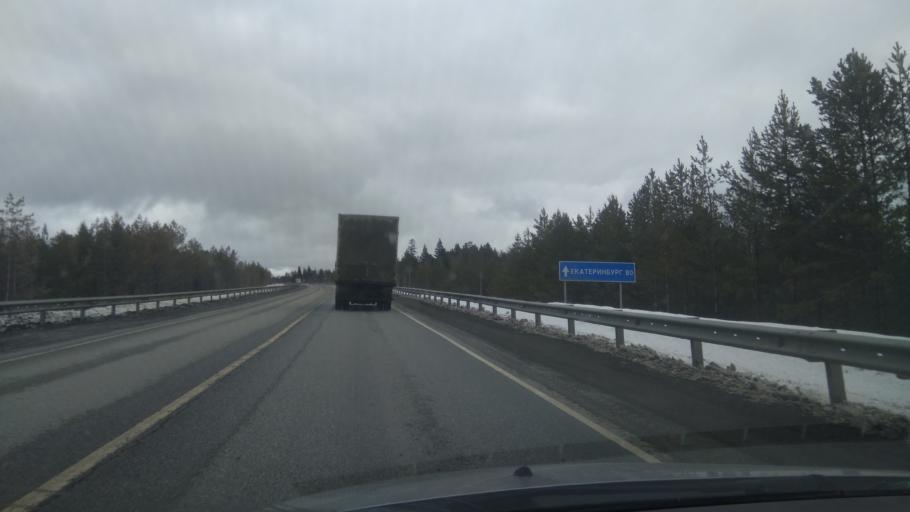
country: RU
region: Sverdlovsk
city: Atig
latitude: 56.7964
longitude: 59.4000
